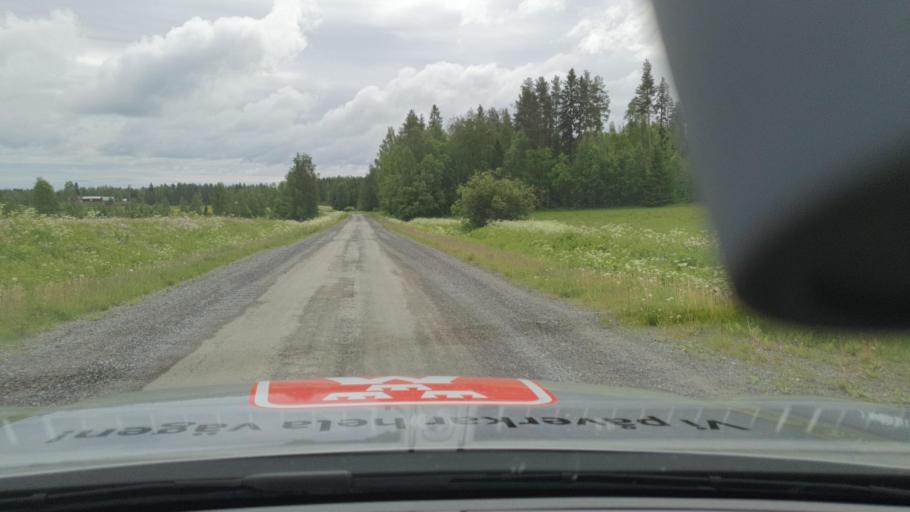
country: SE
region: Norrbotten
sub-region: Lulea Kommun
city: Ranea
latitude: 65.9402
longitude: 22.1173
